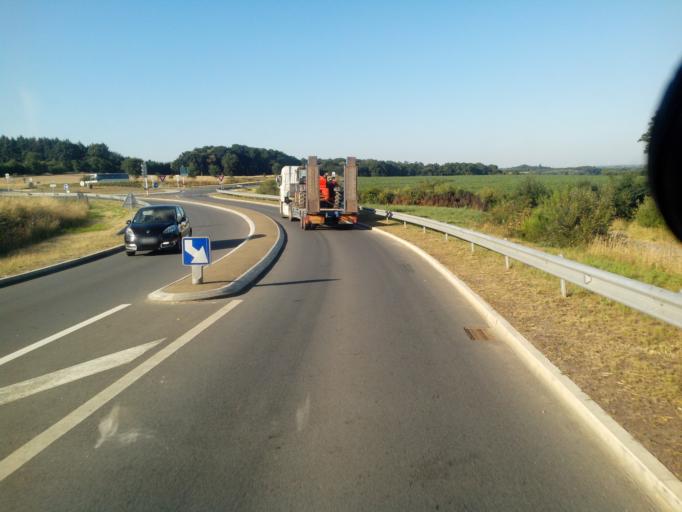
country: FR
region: Brittany
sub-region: Departement du Morbihan
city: Loyat
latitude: 47.9770
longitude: -2.3795
